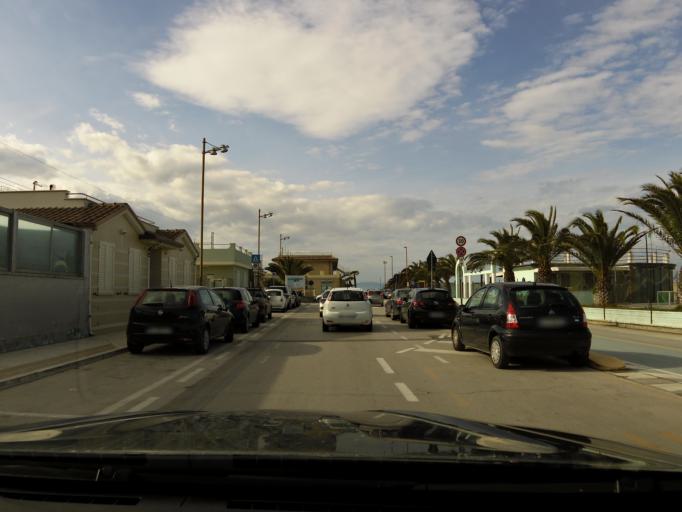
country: IT
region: The Marches
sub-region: Provincia di Macerata
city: Civitanova Marche
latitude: 43.3284
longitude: 13.7148
